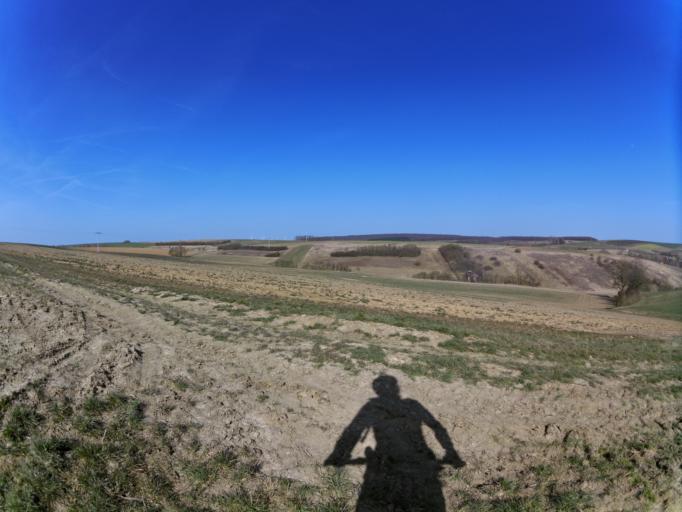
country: DE
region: Bavaria
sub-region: Regierungsbezirk Unterfranken
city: Dettelbach
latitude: 49.8306
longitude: 10.1410
